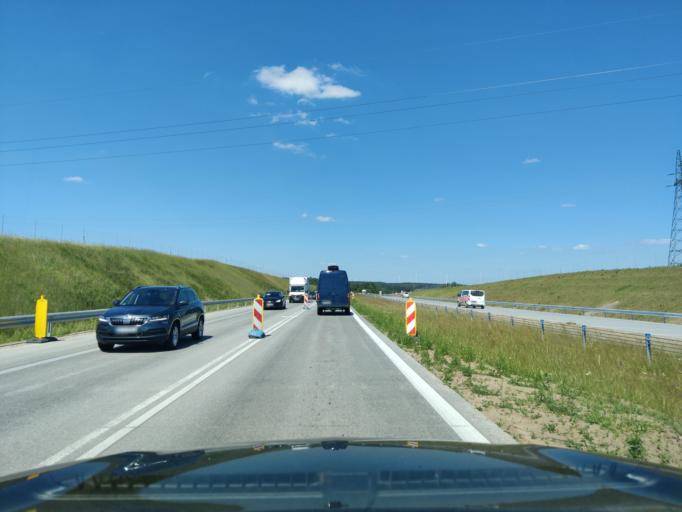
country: PL
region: Masovian Voivodeship
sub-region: Powiat mlawski
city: Mlawa
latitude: 53.1234
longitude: 20.4112
